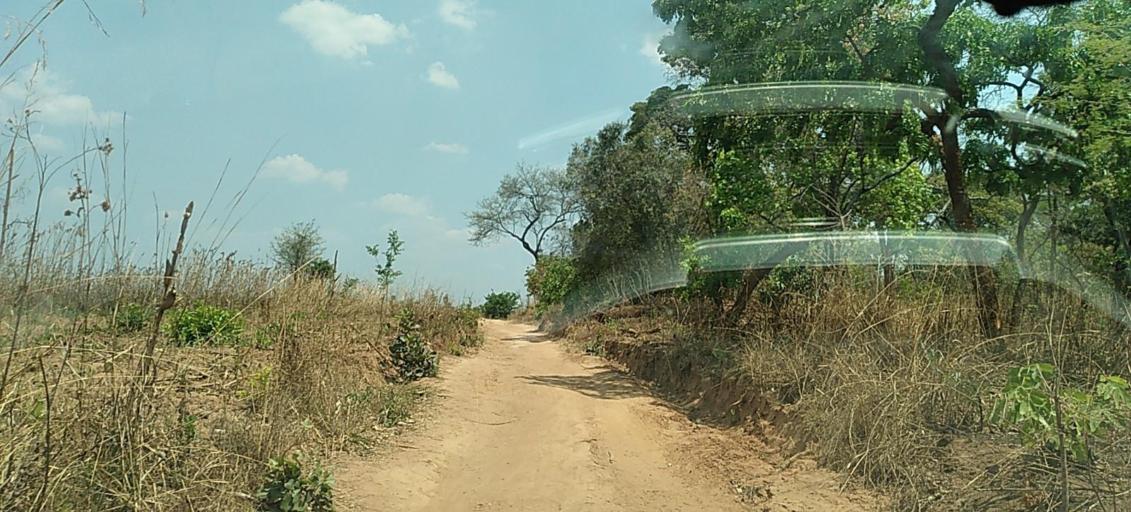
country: ZM
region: North-Western
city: Kasempa
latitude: -13.5307
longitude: 25.8228
